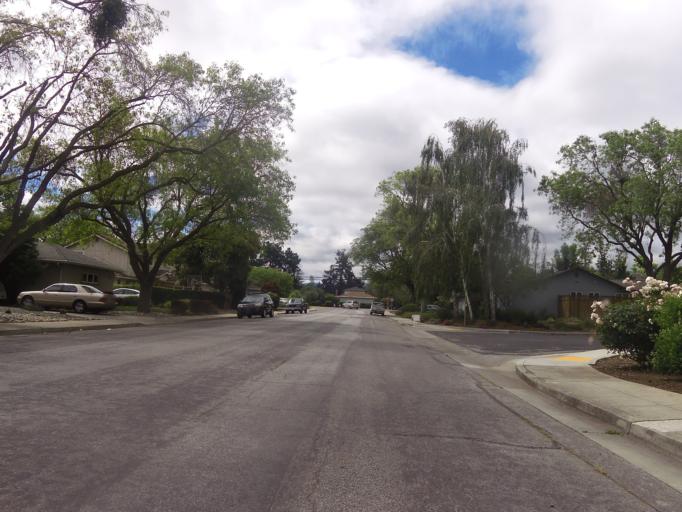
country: US
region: California
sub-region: Santa Clara County
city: Mountain View
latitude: 37.3751
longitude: -122.0913
